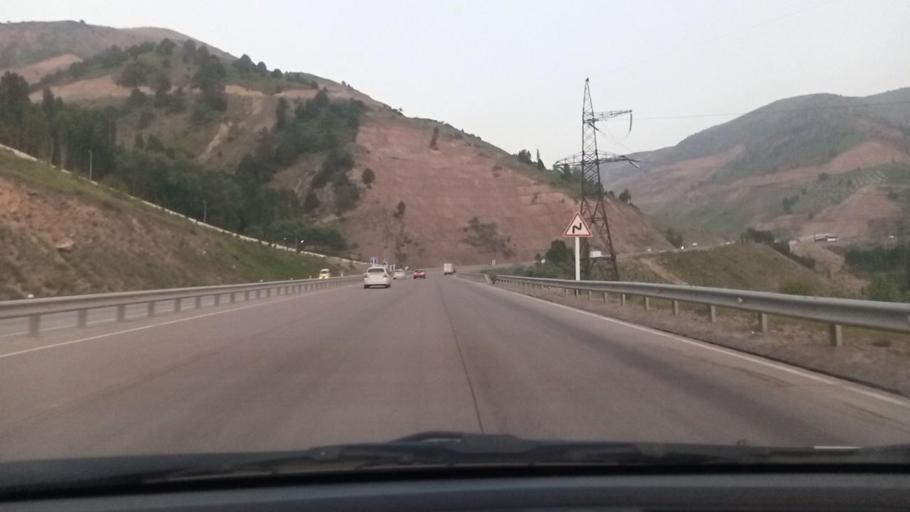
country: UZ
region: Toshkent
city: Angren
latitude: 41.1163
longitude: 70.4950
